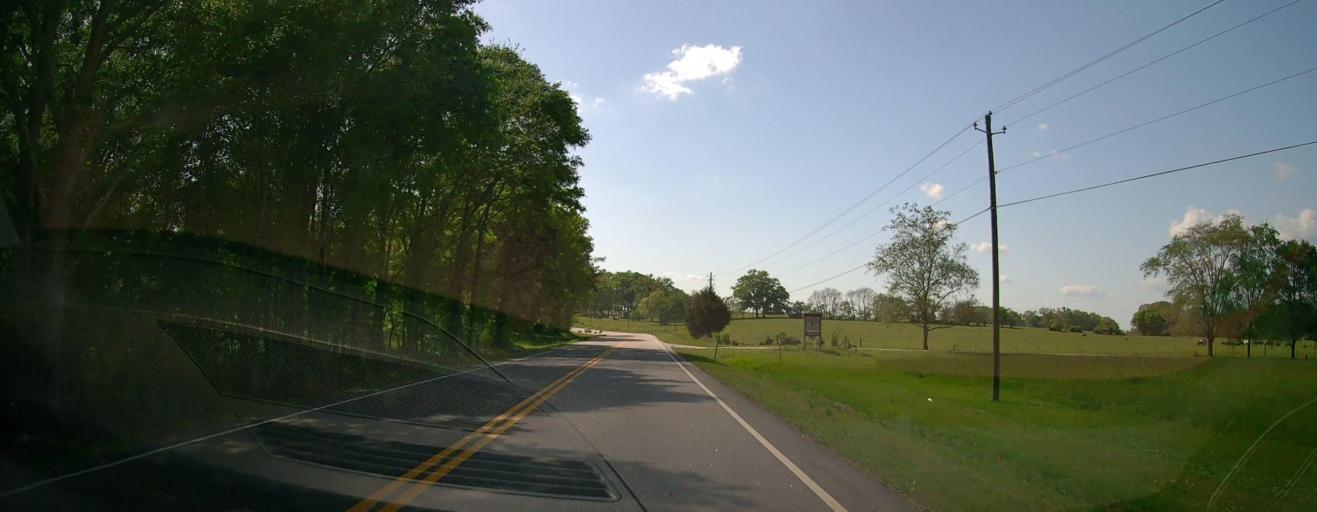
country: US
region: Georgia
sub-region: Morgan County
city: Madison
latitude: 33.6083
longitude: -83.3640
